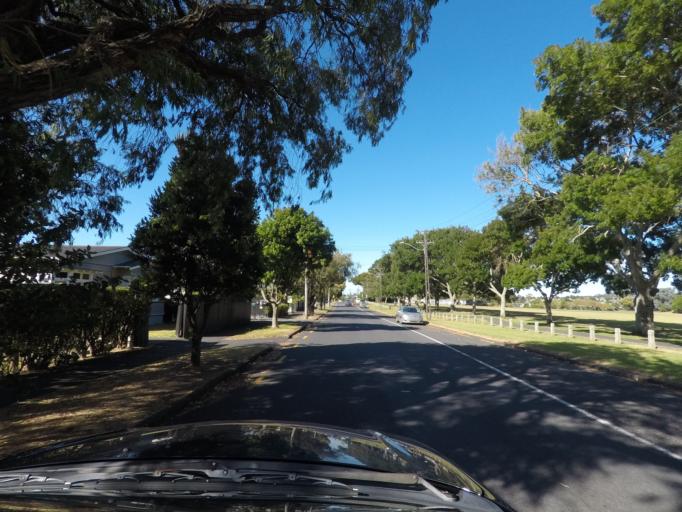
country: NZ
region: Auckland
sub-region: Auckland
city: Rosebank
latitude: -36.8871
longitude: 174.6854
